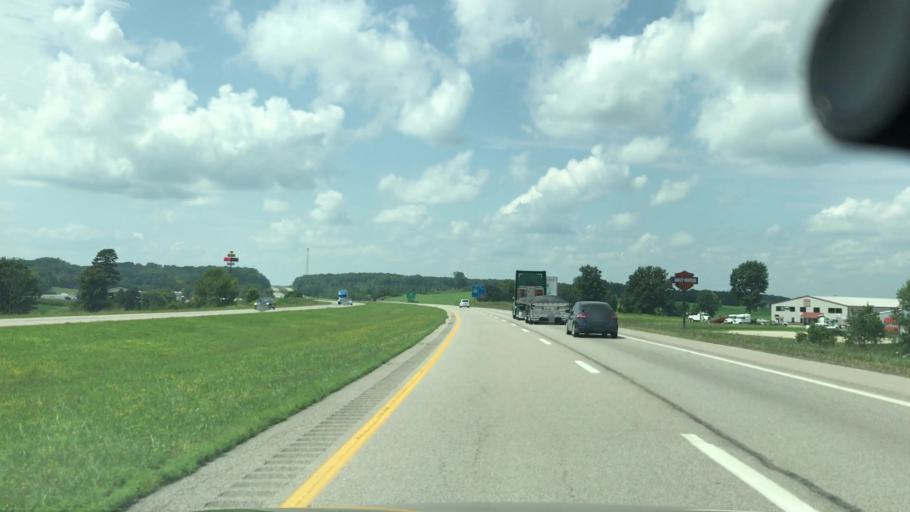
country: US
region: Ohio
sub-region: Gallia County
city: Gallipolis
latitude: 38.8747
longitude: -82.2869
